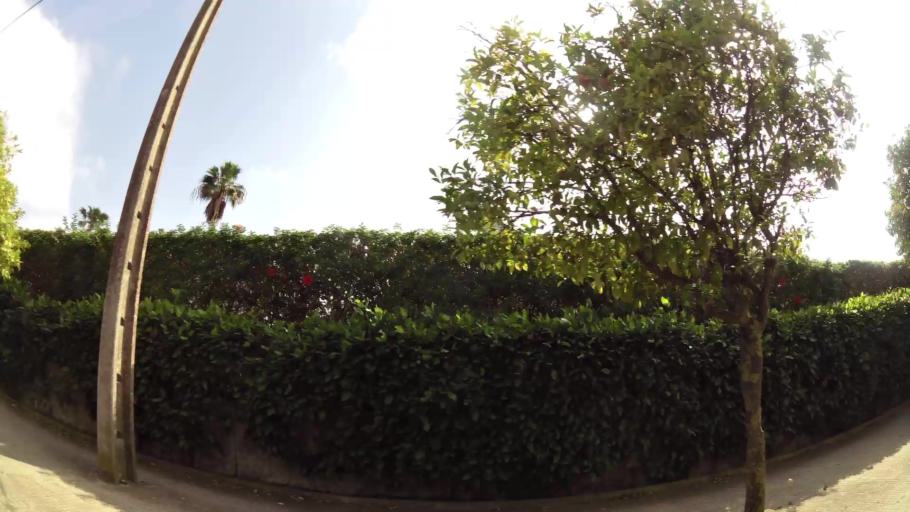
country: MA
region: Rabat-Sale-Zemmour-Zaer
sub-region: Rabat
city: Rabat
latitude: 33.9687
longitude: -6.8549
